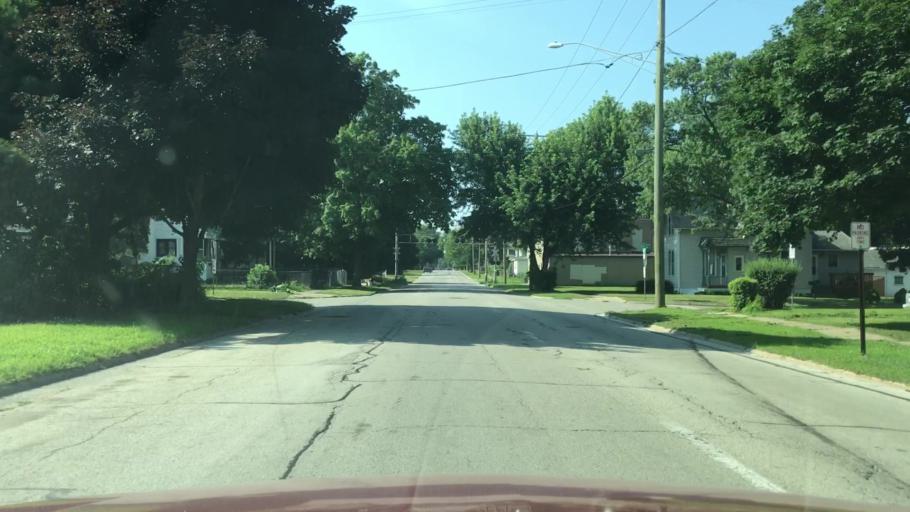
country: US
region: Illinois
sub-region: Winnebago County
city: Rockford
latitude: 42.2566
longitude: -89.0823
